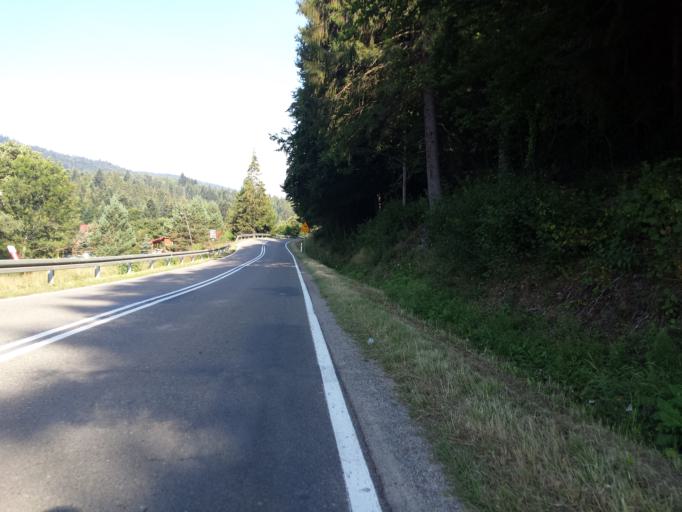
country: PL
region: Subcarpathian Voivodeship
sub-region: Powiat leski
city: Cisna
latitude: 49.2189
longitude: 22.3174
